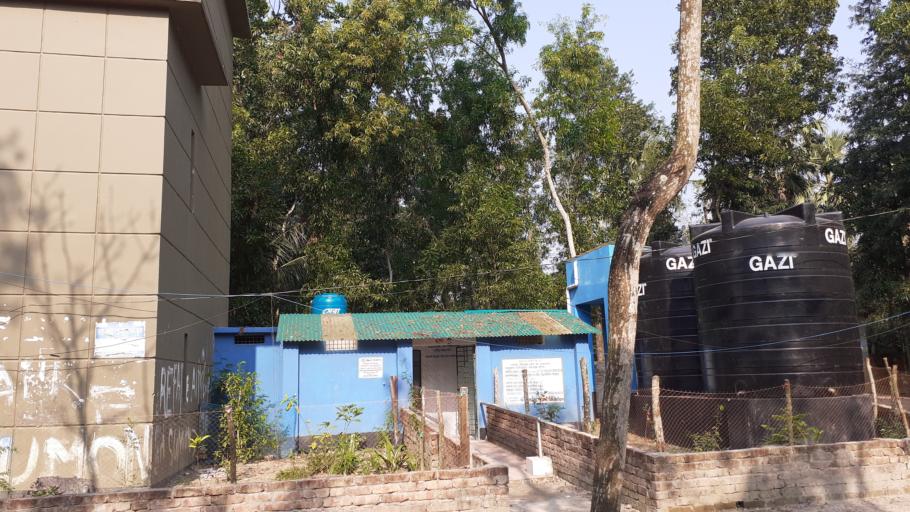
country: IN
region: West Bengal
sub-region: North 24 Parganas
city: Taki
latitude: 22.3792
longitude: 89.1469
